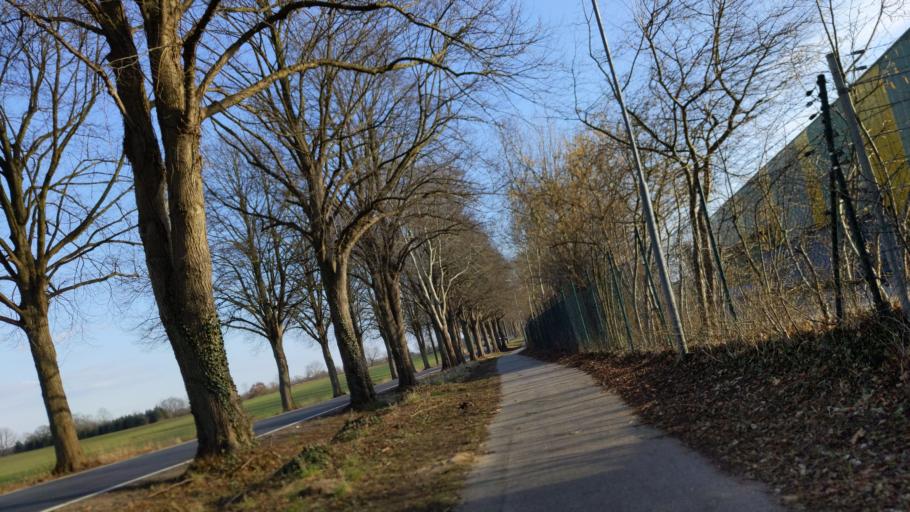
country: DE
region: Schleswig-Holstein
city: Ratekau
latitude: 53.9589
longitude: 10.7230
